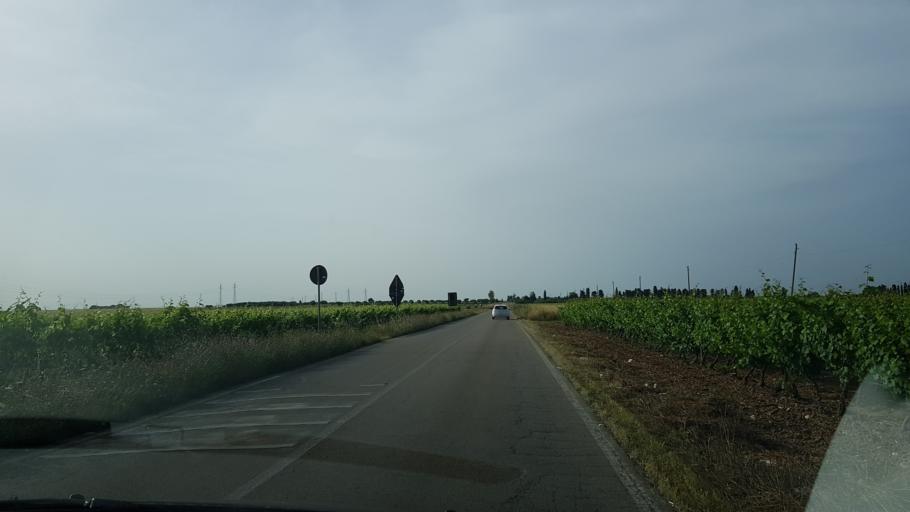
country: IT
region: Apulia
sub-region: Provincia di Brindisi
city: San Pancrazio Salentino
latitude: 40.3776
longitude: 17.8375
